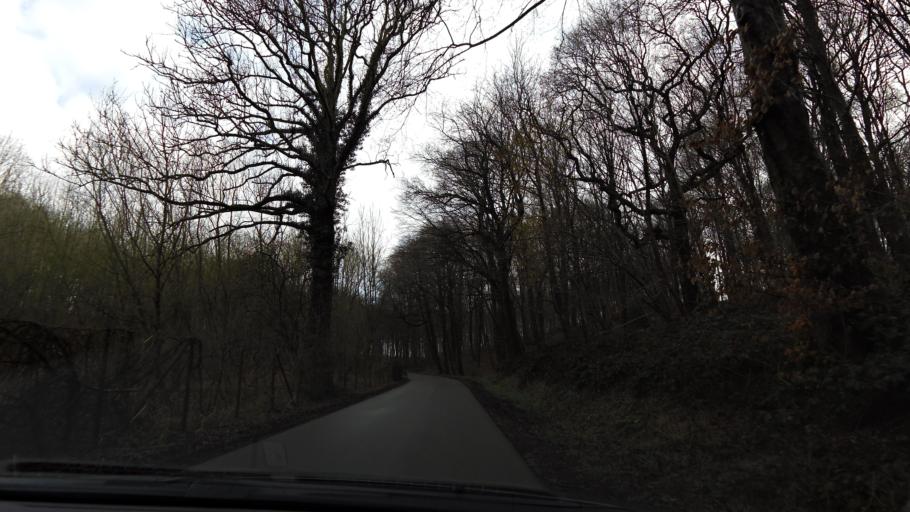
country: BE
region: Wallonia
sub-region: Province de Liege
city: Aubel
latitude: 50.7604
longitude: 5.8838
